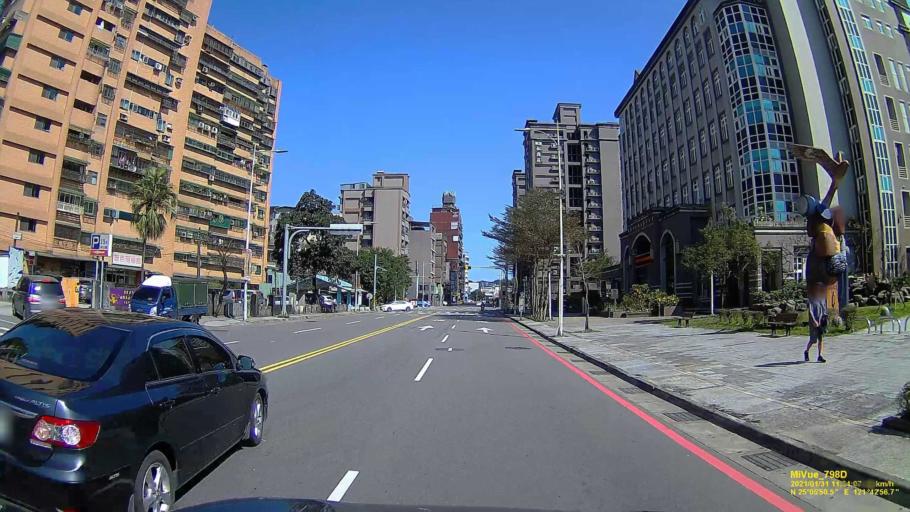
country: TW
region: Taiwan
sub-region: Keelung
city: Keelung
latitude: 25.0975
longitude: 121.7159
